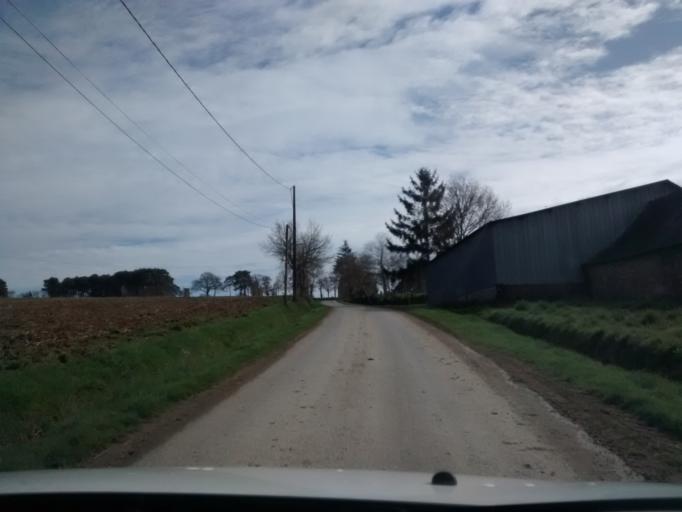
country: FR
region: Brittany
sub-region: Departement d'Ille-et-Vilaine
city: Liffre
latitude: 48.1941
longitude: -1.4921
